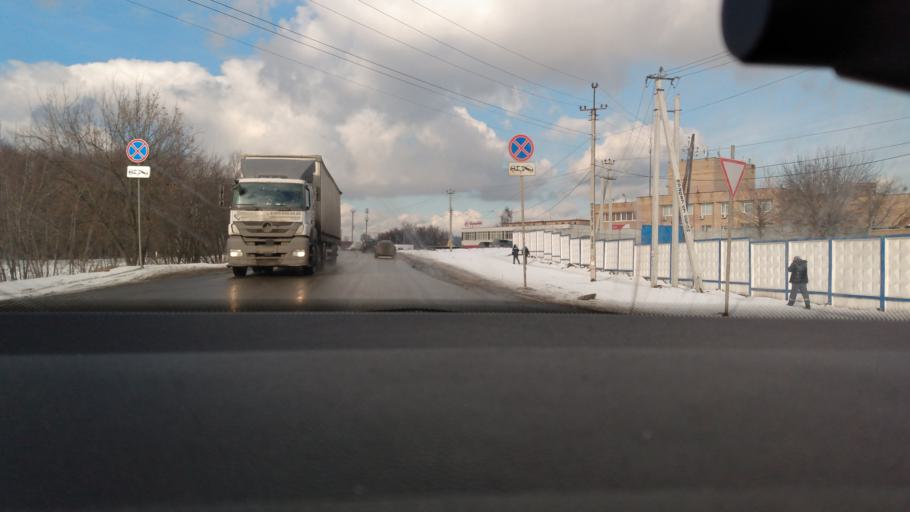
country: RU
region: Moskovskaya
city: Zheleznodorozhnyy
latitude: 55.7218
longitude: 38.0429
